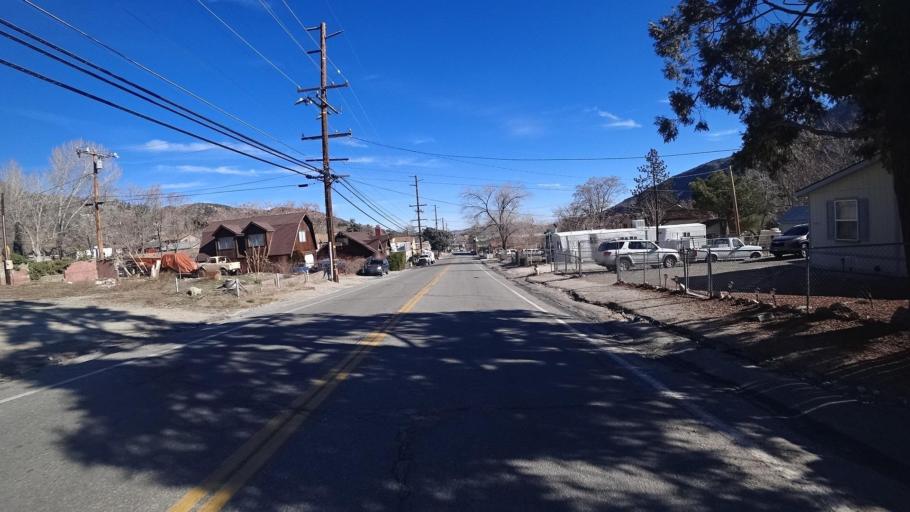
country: US
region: California
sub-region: Kern County
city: Frazier Park
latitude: 34.8227
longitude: -118.9483
